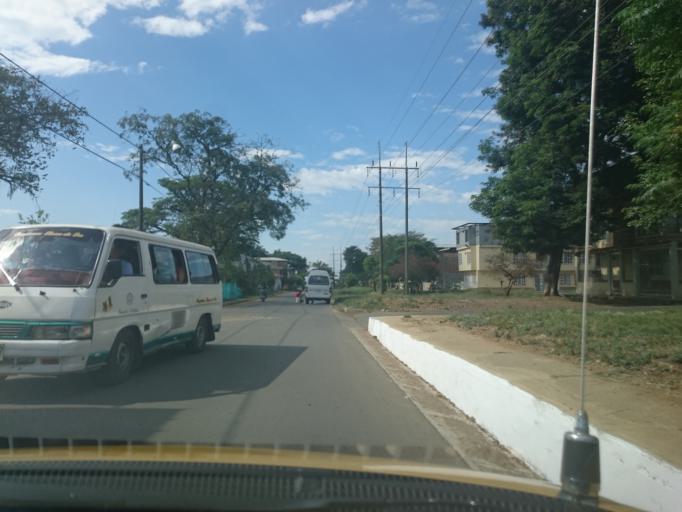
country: CO
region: Cauca
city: Santander de Quilichao
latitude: 3.0137
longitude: -76.4884
